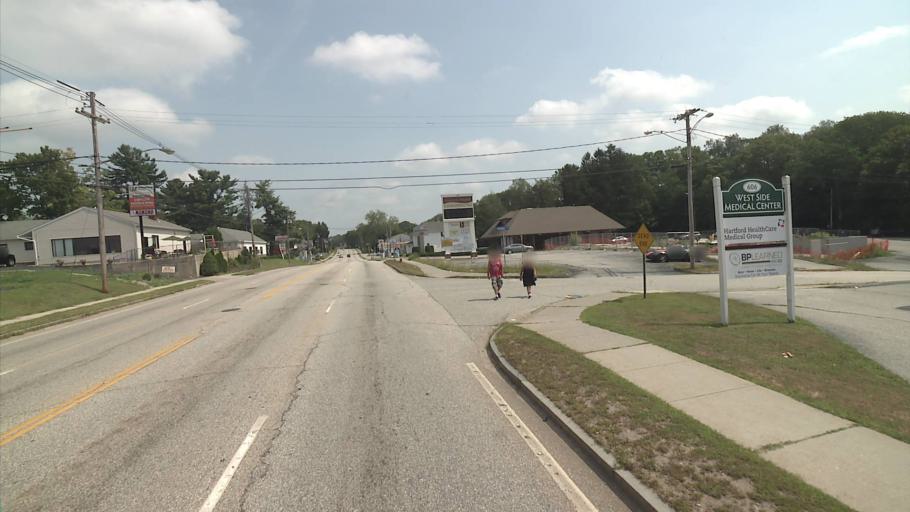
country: US
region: Connecticut
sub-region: New London County
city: Norwich
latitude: 41.5161
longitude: -72.1006
